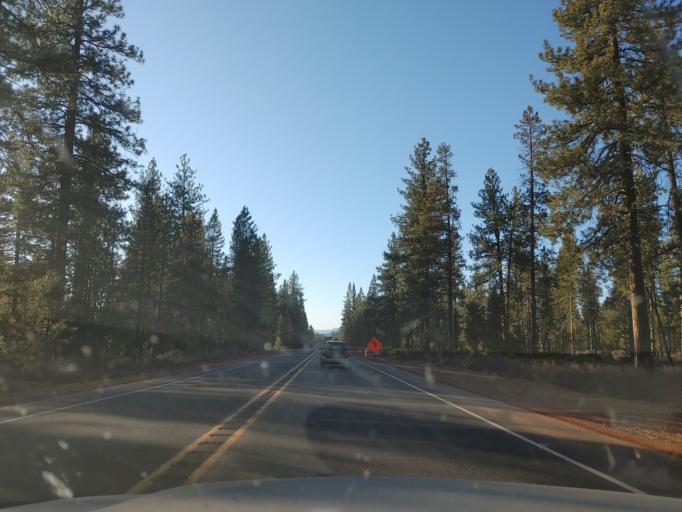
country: US
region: Oregon
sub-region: Deschutes County
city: La Pine
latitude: 43.3743
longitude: -121.7950
